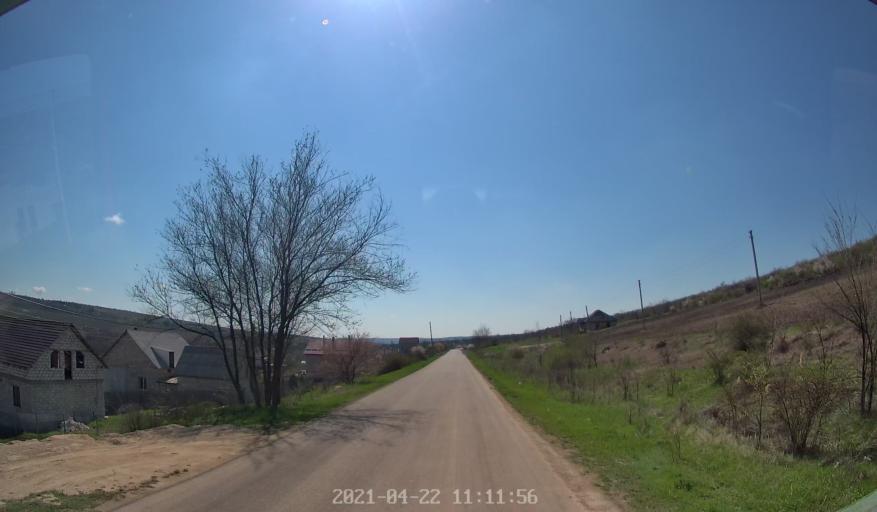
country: MD
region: Chisinau
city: Ciorescu
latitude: 47.1573
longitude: 28.9563
